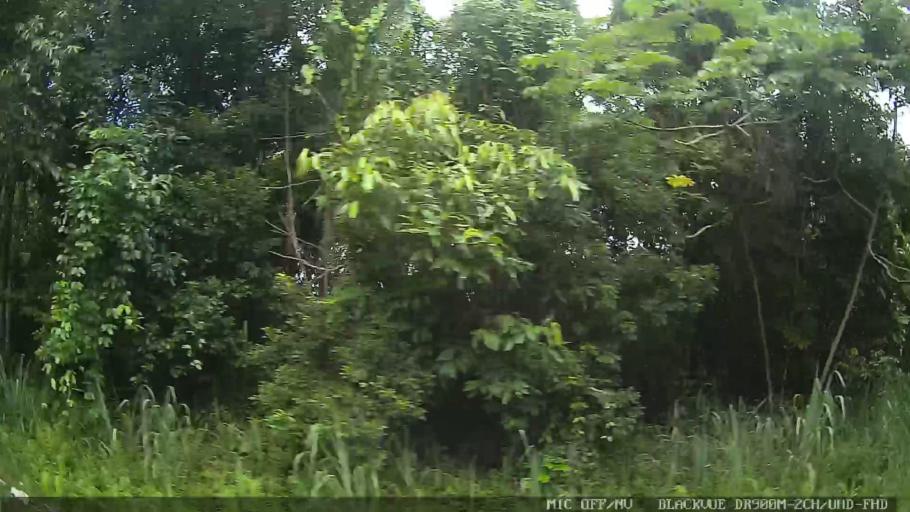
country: BR
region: Sao Paulo
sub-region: Iguape
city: Iguape
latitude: -24.6741
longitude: -47.4502
